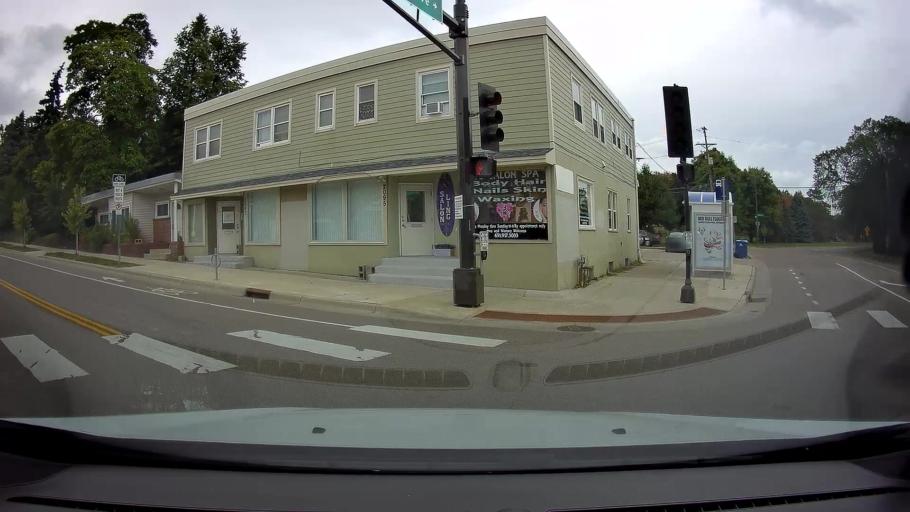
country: US
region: Minnesota
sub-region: Ramsey County
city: Lauderdale
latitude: 44.9769
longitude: -93.1895
